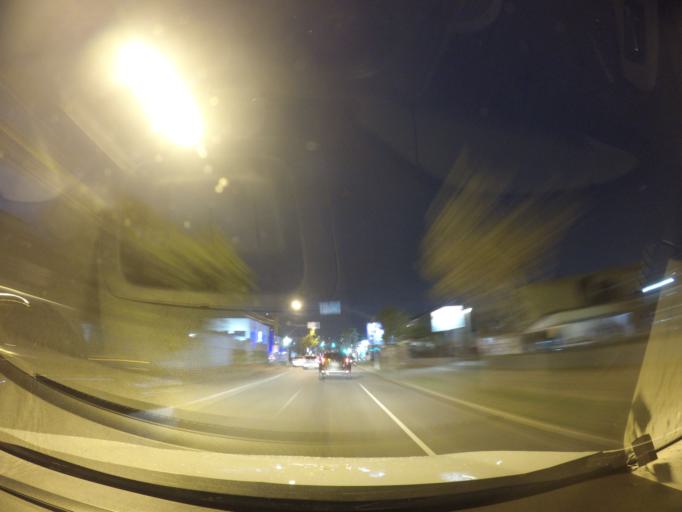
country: BR
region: Parana
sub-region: Curitiba
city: Curitiba
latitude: -25.4539
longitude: -49.2707
